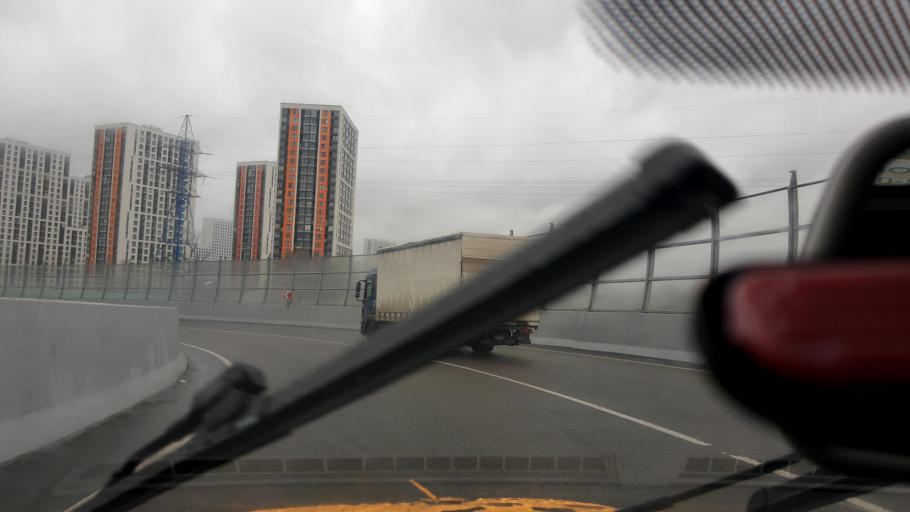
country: RU
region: Moskovskaya
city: Odintsovo
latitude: 55.6533
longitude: 37.2761
